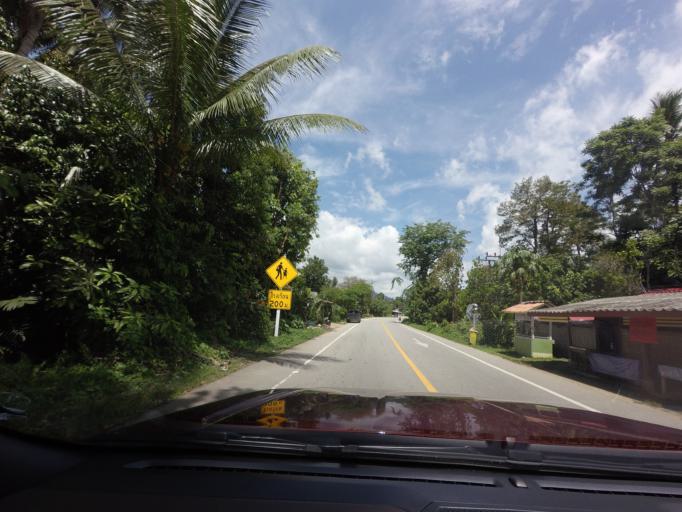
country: TH
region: Narathiwat
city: Ra-ngae
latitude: 6.2399
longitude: 101.6781
